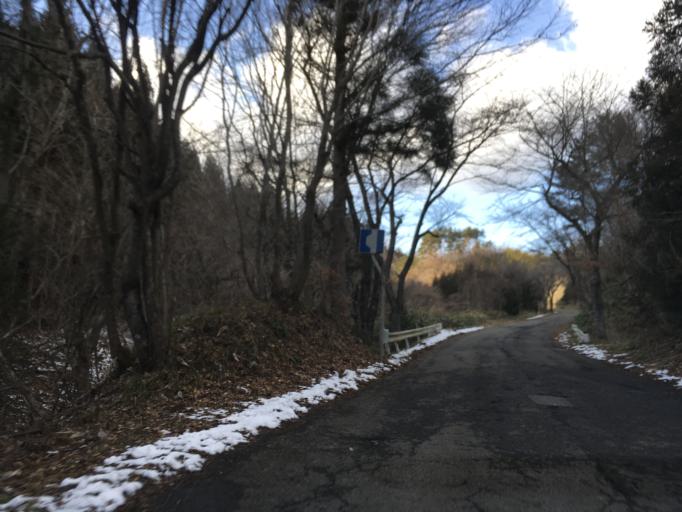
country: JP
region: Miyagi
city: Furukawa
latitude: 38.8163
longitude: 140.8332
